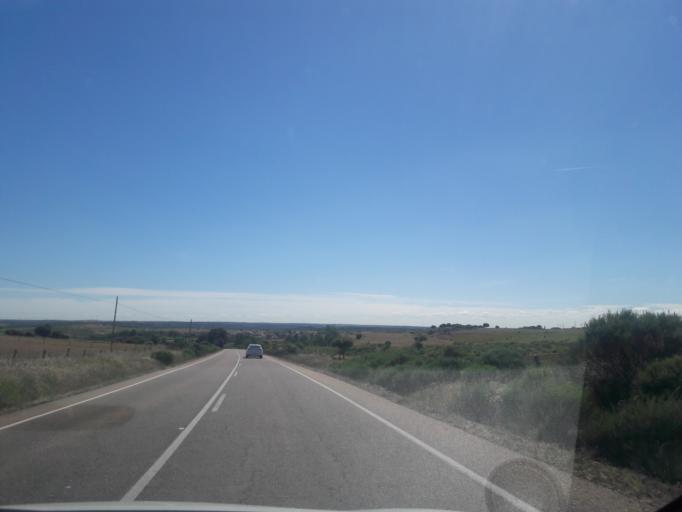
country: ES
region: Castille and Leon
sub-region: Provincia de Salamanca
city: Cerralbo
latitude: 40.9713
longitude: -6.6030
